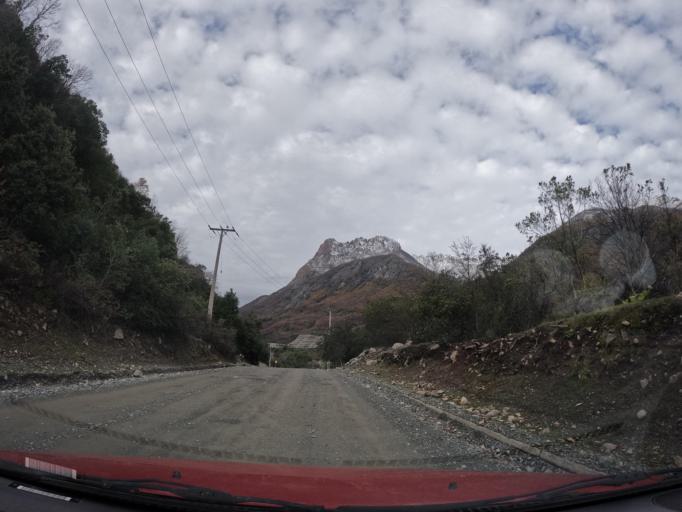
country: CL
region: Maule
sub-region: Provincia de Linares
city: Colbun
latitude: -35.8582
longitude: -71.2163
